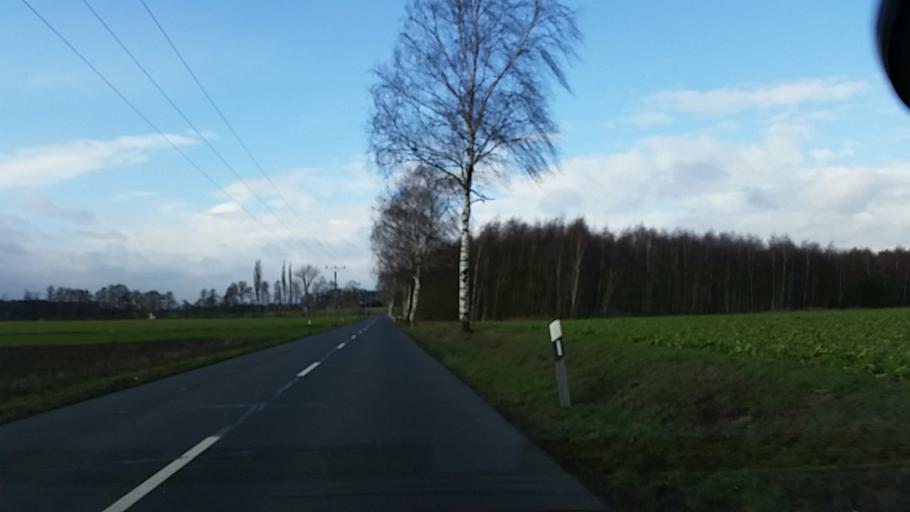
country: DE
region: Lower Saxony
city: Wrestedt
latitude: 52.9089
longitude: 10.5509
